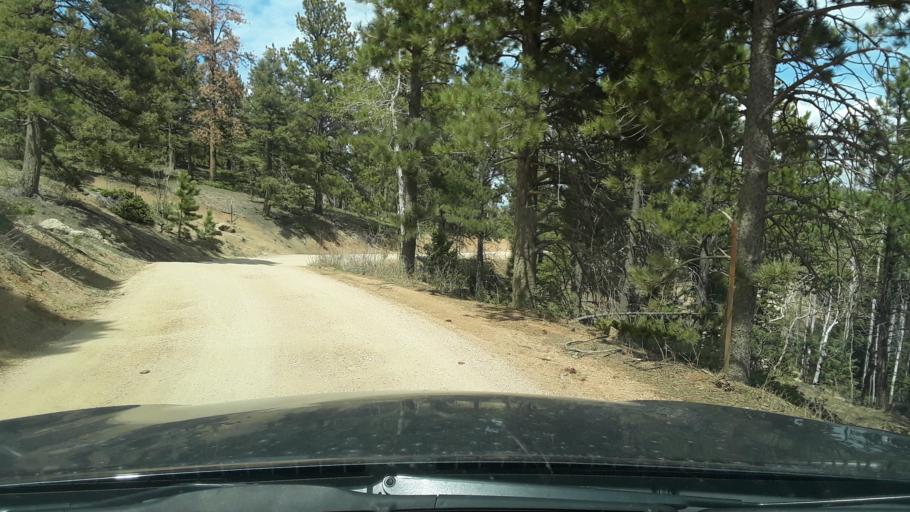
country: US
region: Colorado
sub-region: El Paso County
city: Palmer Lake
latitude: 39.0704
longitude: -104.9509
